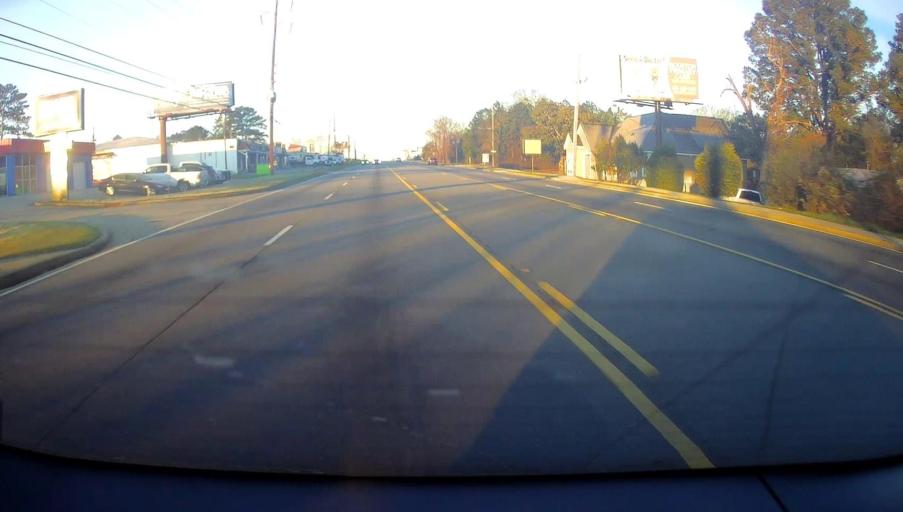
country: US
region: Georgia
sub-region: Houston County
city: Centerville
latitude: 32.6189
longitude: -83.6621
